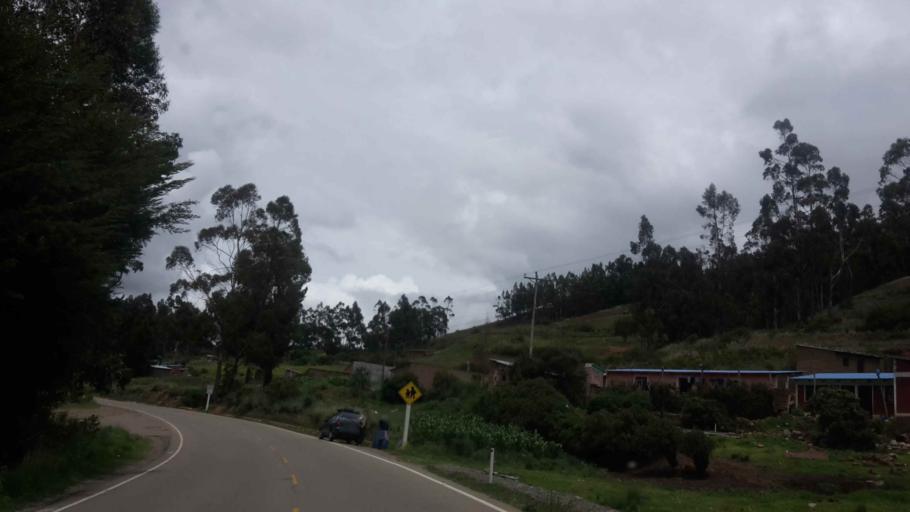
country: BO
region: Cochabamba
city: Arani
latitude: -17.4916
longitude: -65.4519
